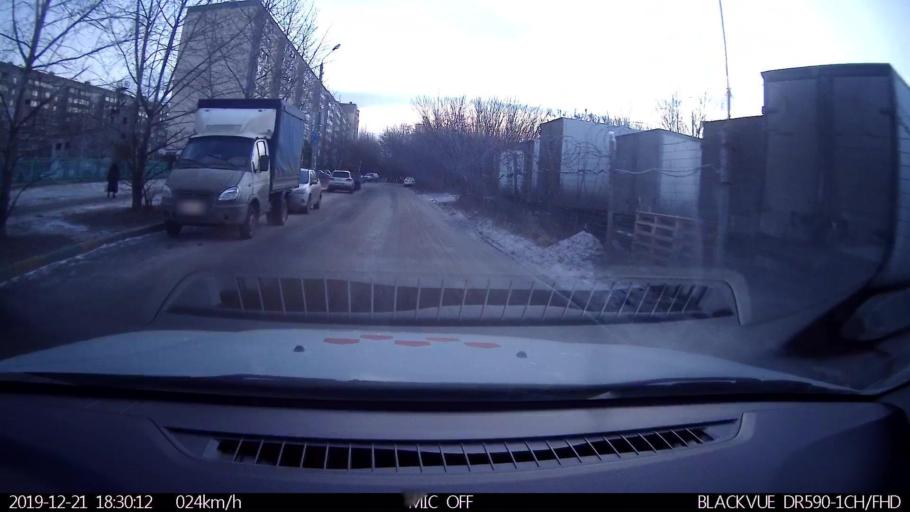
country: RU
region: Nizjnij Novgorod
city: Nizhniy Novgorod
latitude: 56.3361
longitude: 43.9140
